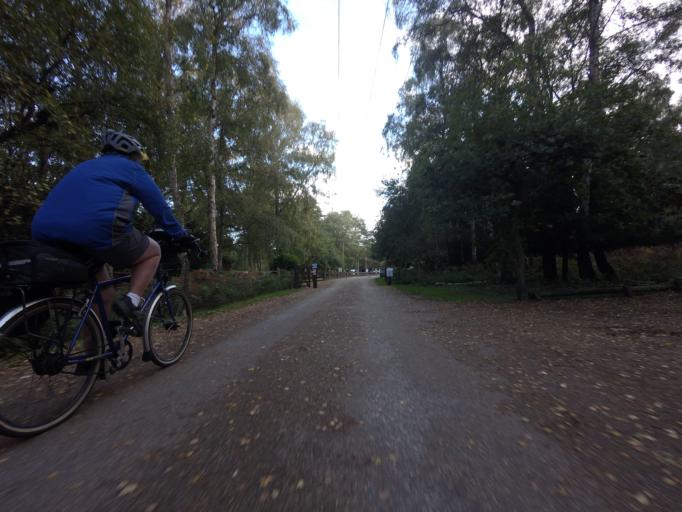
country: GB
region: England
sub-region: Norfolk
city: Dersingham
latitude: 52.8174
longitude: 0.4944
